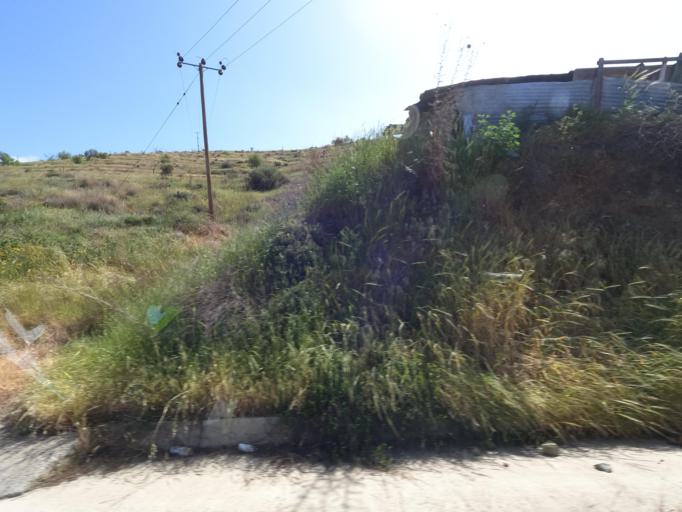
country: CY
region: Lefkosia
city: Astromeritis
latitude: 35.0711
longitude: 33.0181
